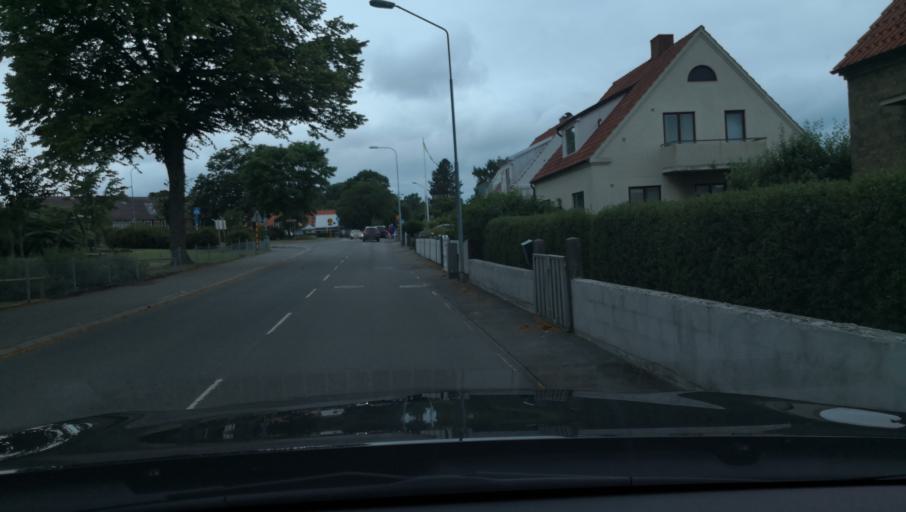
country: SE
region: Skane
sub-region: Simrishamns Kommun
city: Kivik
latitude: 55.6845
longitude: 14.2281
